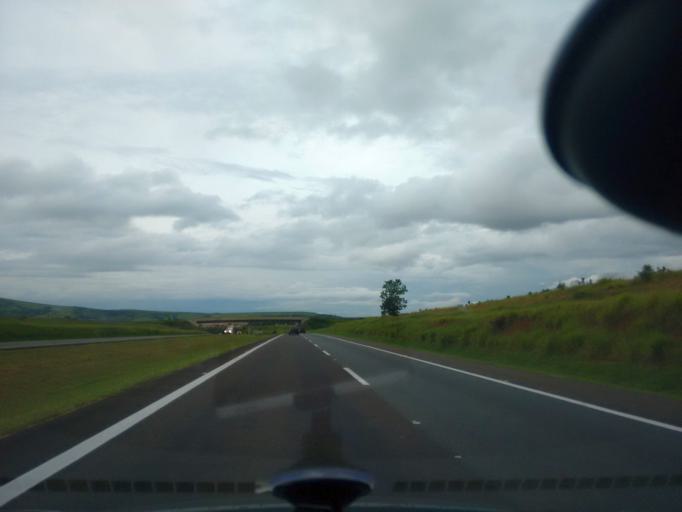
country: BR
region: Sao Paulo
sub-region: Limeira
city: Limeira
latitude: -22.5732
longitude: -47.4579
